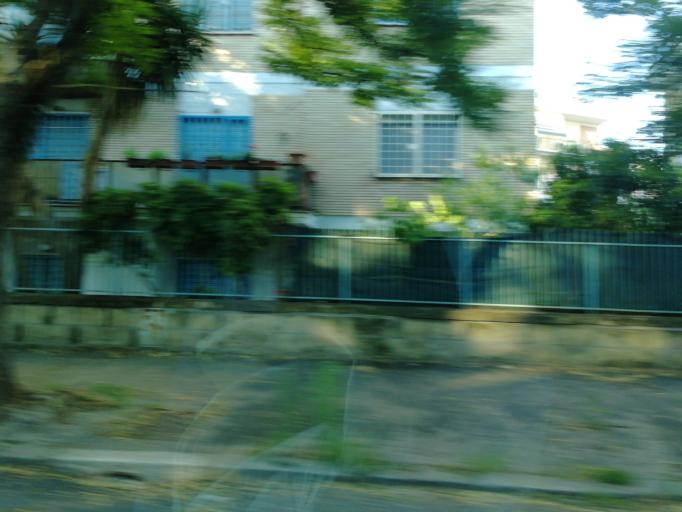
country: IT
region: Latium
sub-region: Citta metropolitana di Roma Capitale
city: Rome
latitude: 41.8616
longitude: 12.5464
